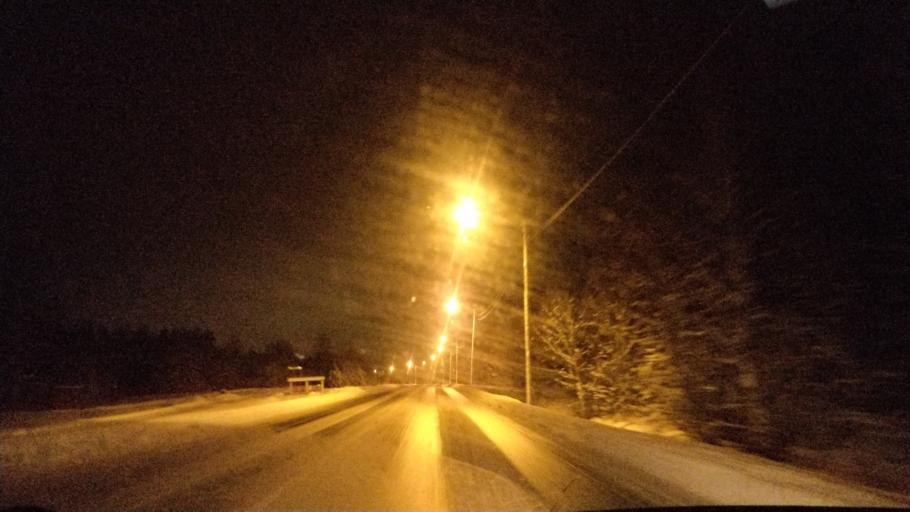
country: FI
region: Lapland
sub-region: Rovaniemi
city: Rovaniemi
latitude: 66.3897
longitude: 25.3783
